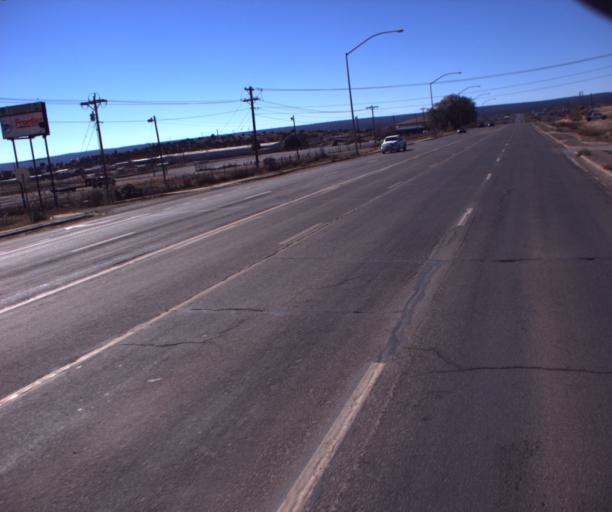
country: US
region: Arizona
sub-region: Apache County
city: Window Rock
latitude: 35.6624
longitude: -109.0634
